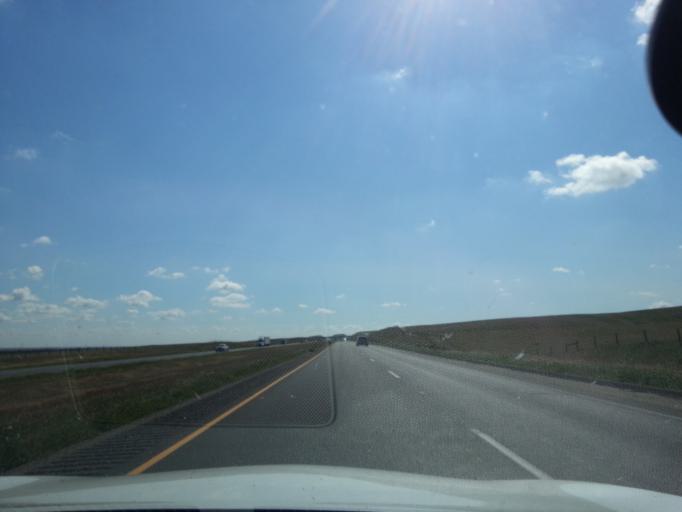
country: US
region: California
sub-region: Fresno County
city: Coalinga
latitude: 36.3401
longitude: -120.3089
